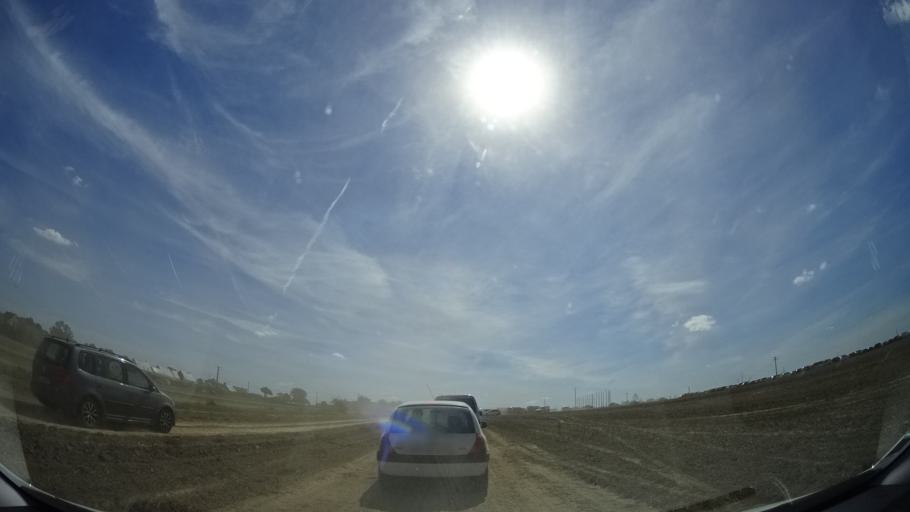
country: FR
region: Brittany
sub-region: Departement d'Ille-et-Vilaine
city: Javene
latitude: 48.3205
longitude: -1.2232
